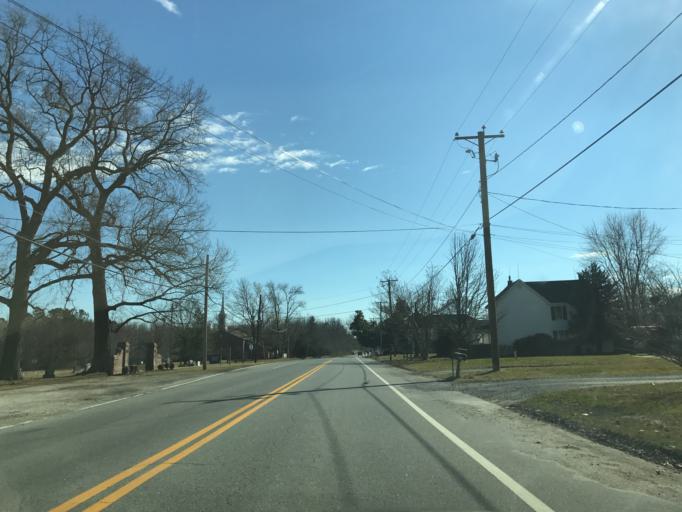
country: US
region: Maryland
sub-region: Queen Anne's County
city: Chester
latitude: 38.9676
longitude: -76.2780
